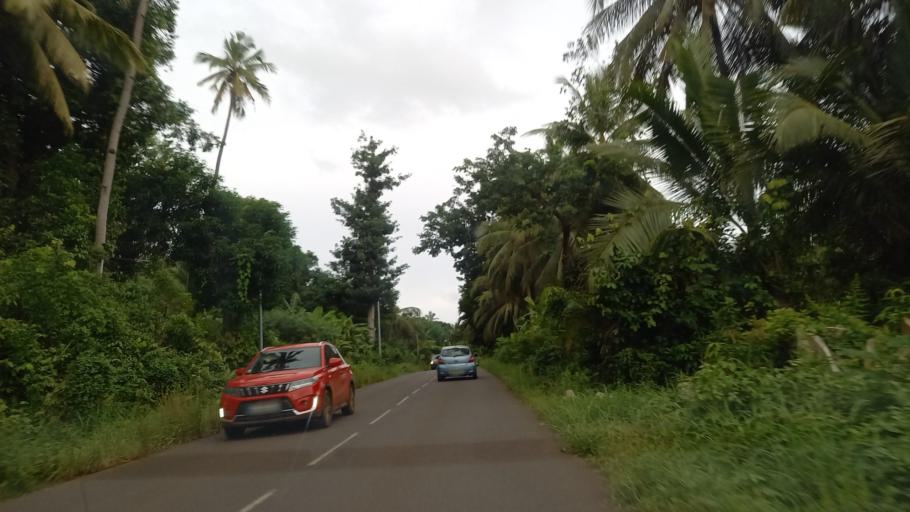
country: YT
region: Sada
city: Sada
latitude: -12.8736
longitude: 45.1198
